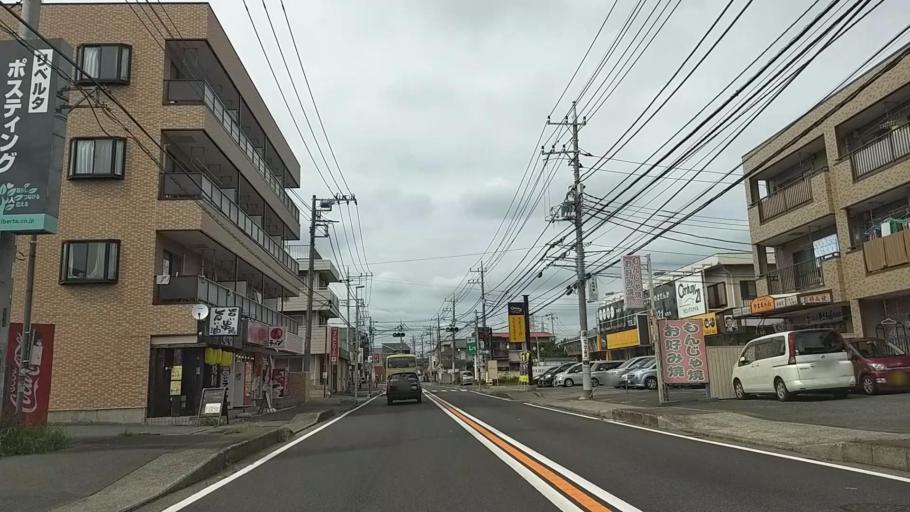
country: JP
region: Kanagawa
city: Minami-rinkan
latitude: 35.4605
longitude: 139.4674
